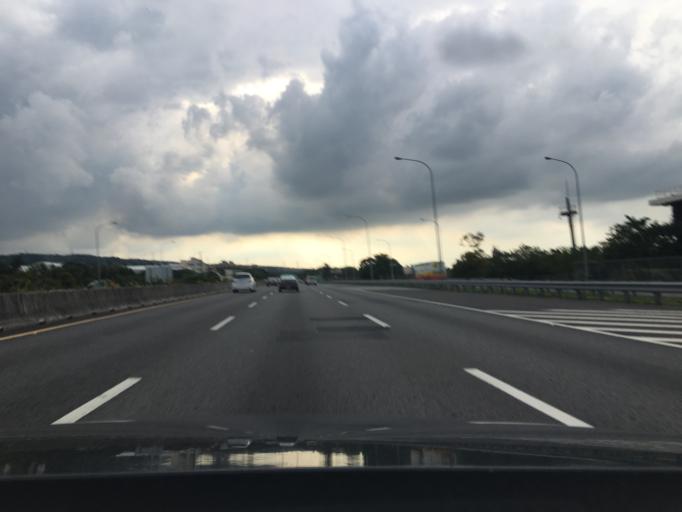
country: TW
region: Taiwan
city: Daxi
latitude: 24.8995
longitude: 121.1473
